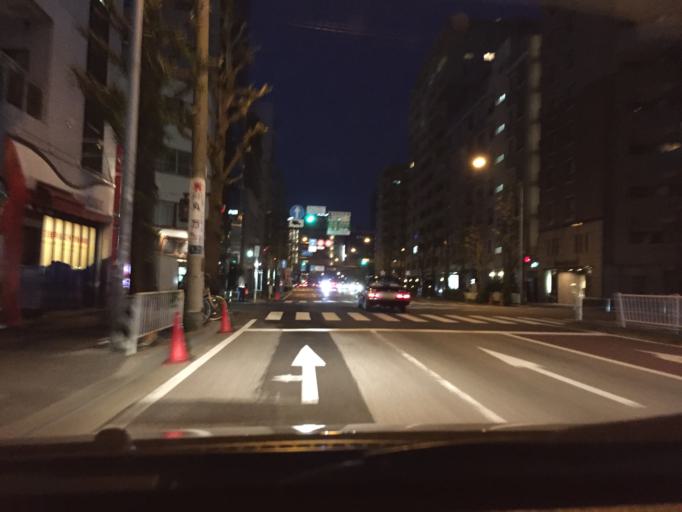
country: JP
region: Kanagawa
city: Yokohama
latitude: 35.4401
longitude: 139.6380
